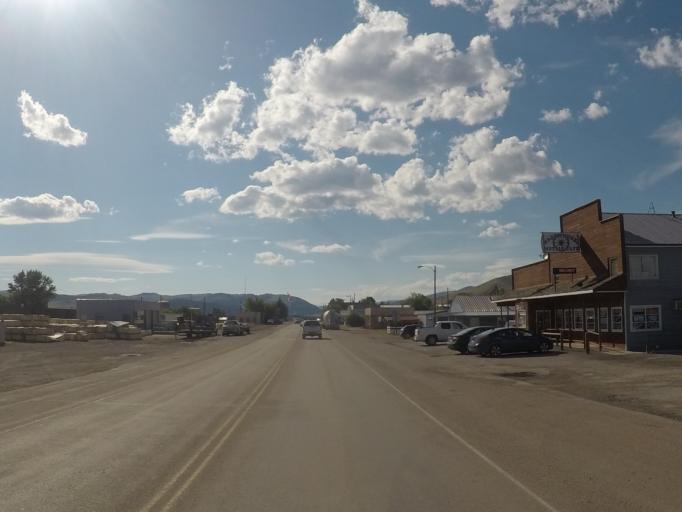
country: US
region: Montana
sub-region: Granite County
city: Philipsburg
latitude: 46.6657
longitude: -113.1421
